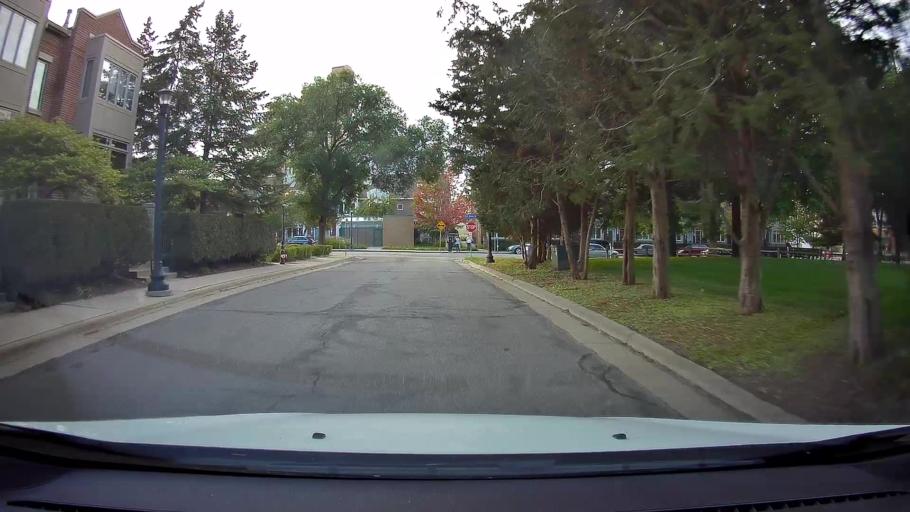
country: US
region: Minnesota
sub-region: Hennepin County
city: Minneapolis
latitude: 44.9865
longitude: -93.2558
